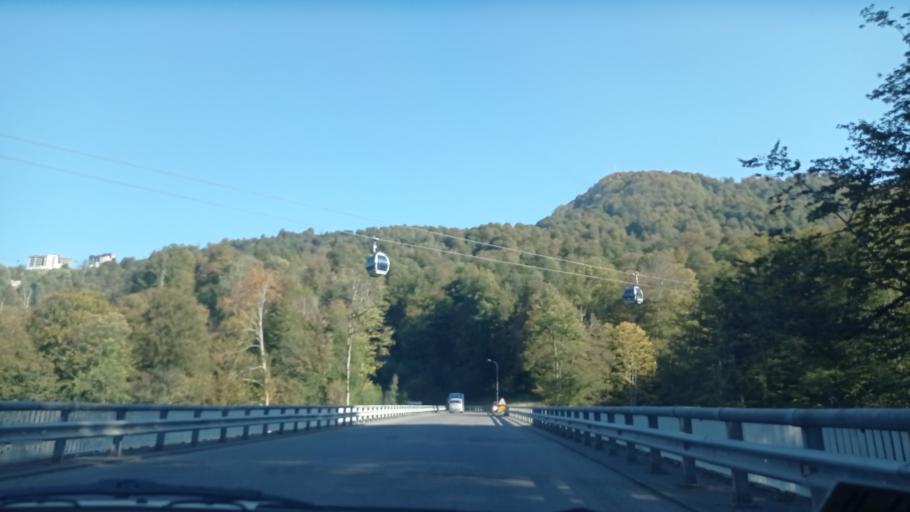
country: RU
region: Krasnodarskiy
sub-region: Sochi City
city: Krasnaya Polyana
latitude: 43.6593
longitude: 40.3008
